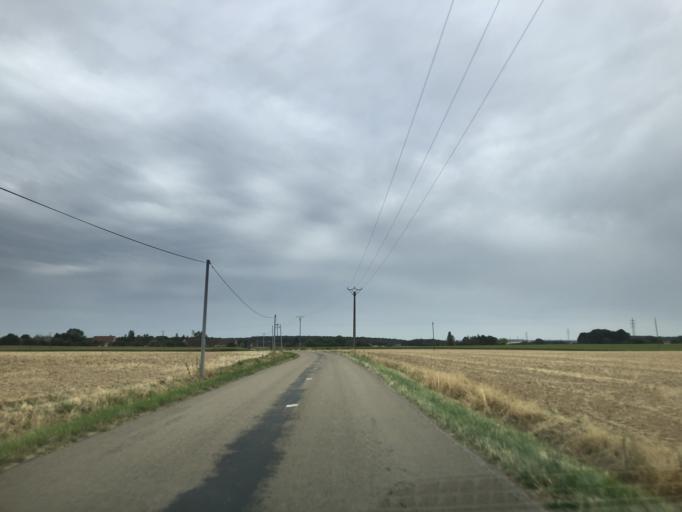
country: FR
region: Centre
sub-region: Departement du Loiret
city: Douchy
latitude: 47.9792
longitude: 3.1422
